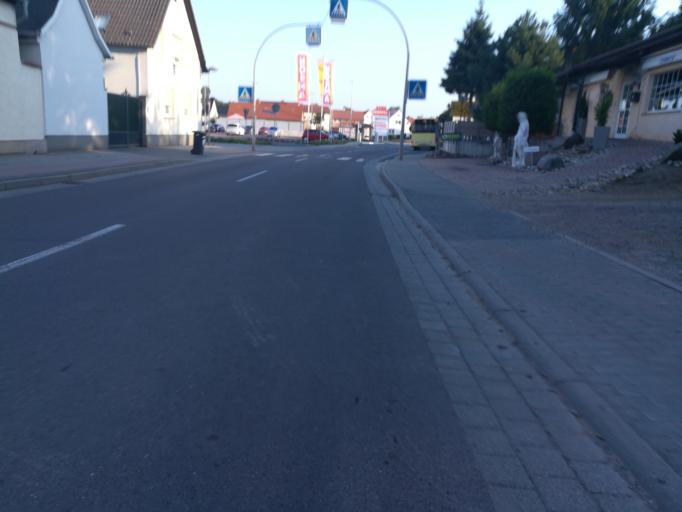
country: DE
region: Saxony-Anhalt
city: Irxleben
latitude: 52.1650
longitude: 11.4833
